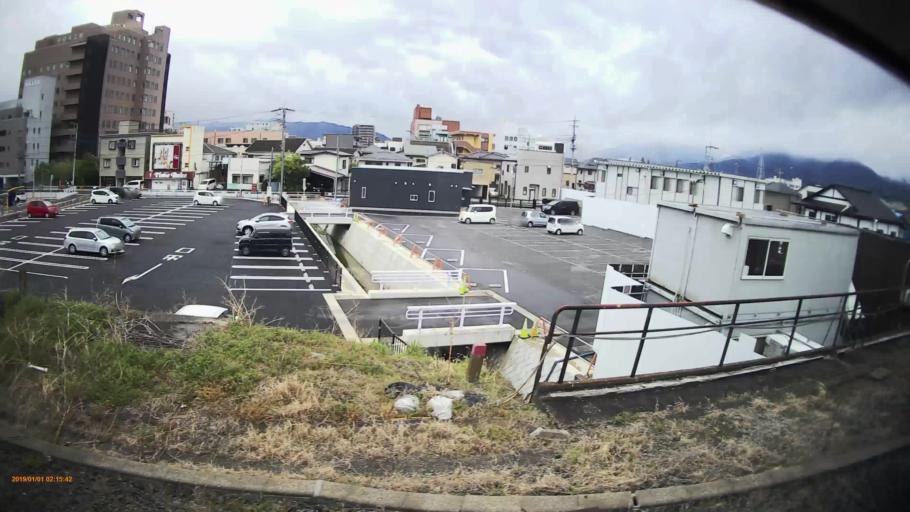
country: JP
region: Yamanashi
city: Kofu-shi
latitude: 35.6683
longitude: 138.5639
